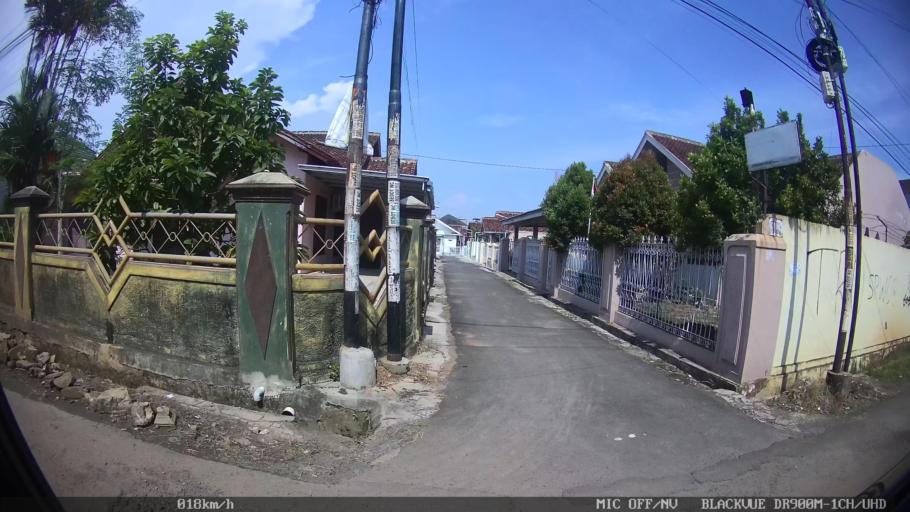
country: ID
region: Lampung
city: Kedaton
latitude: -5.3921
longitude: 105.2445
